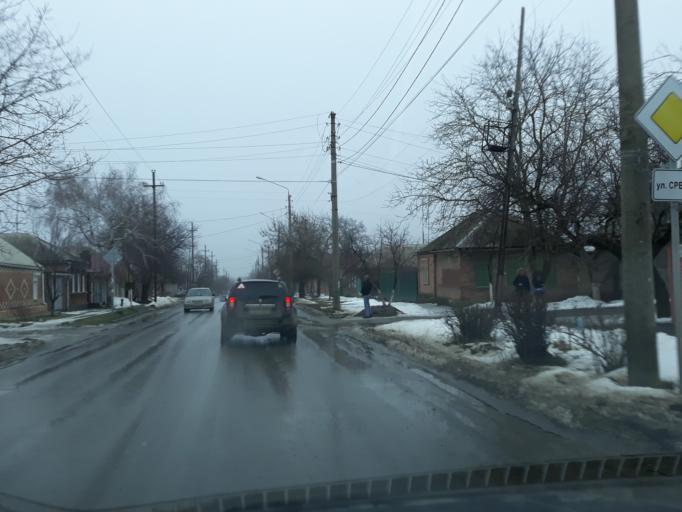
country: RU
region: Rostov
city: Taganrog
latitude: 47.2101
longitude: 38.8966
